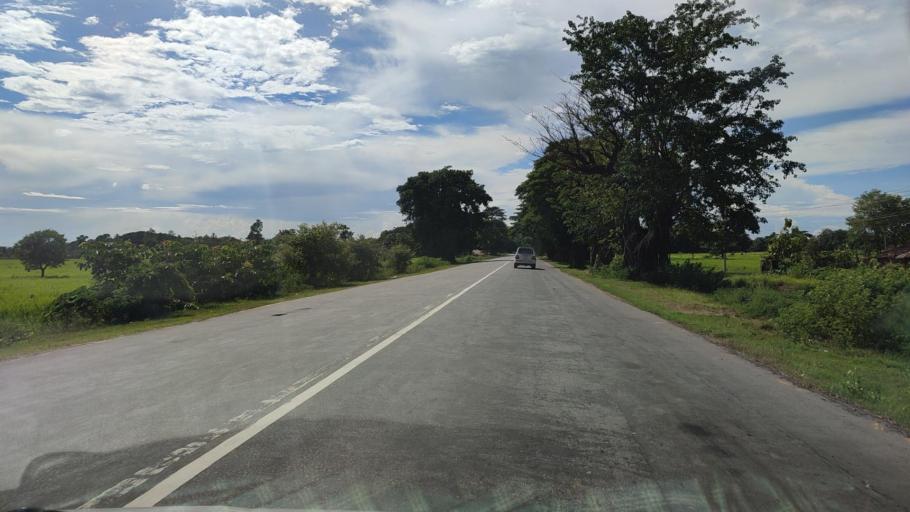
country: MM
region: Bago
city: Pyu
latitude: 18.2367
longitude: 96.5502
